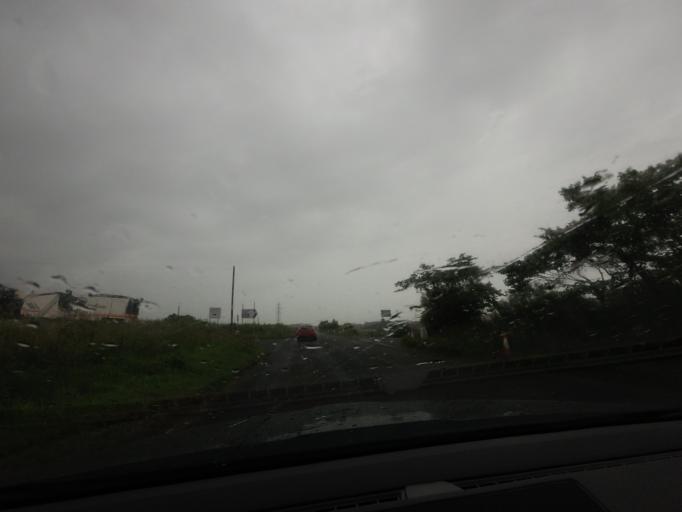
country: GB
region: Scotland
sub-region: Aberdeenshire
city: Mintlaw
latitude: 57.6119
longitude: -1.9485
